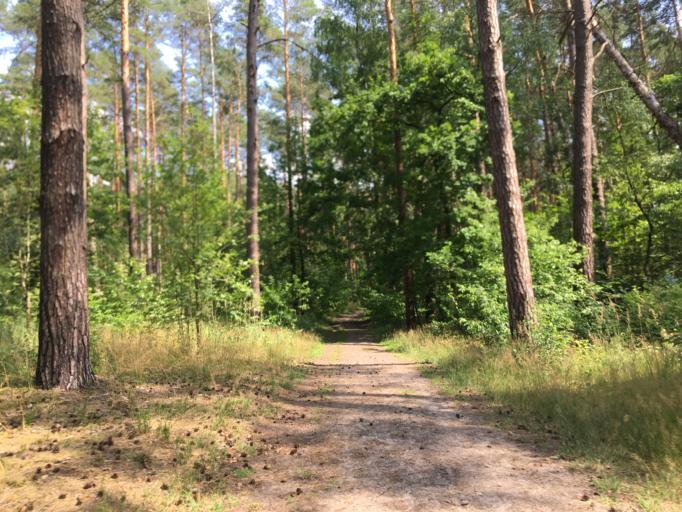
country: DE
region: Brandenburg
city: Glienicke
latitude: 52.6751
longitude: 13.3350
